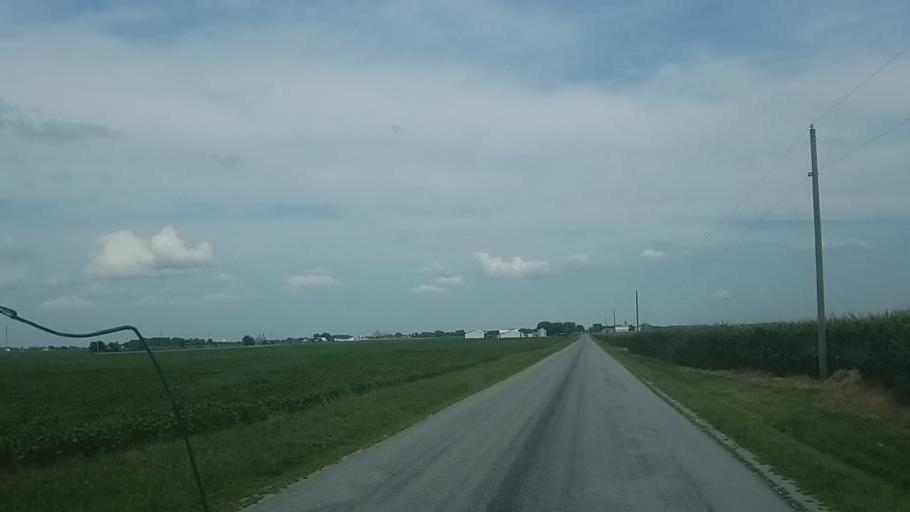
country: US
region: Ohio
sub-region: Wyandot County
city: Upper Sandusky
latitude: 40.8178
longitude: -83.3377
